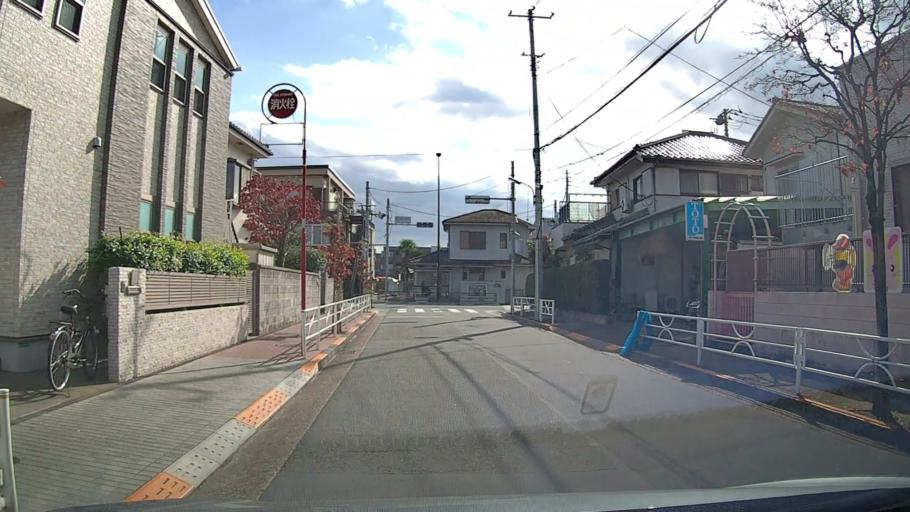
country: JP
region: Saitama
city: Wako
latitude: 35.7515
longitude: 139.6309
